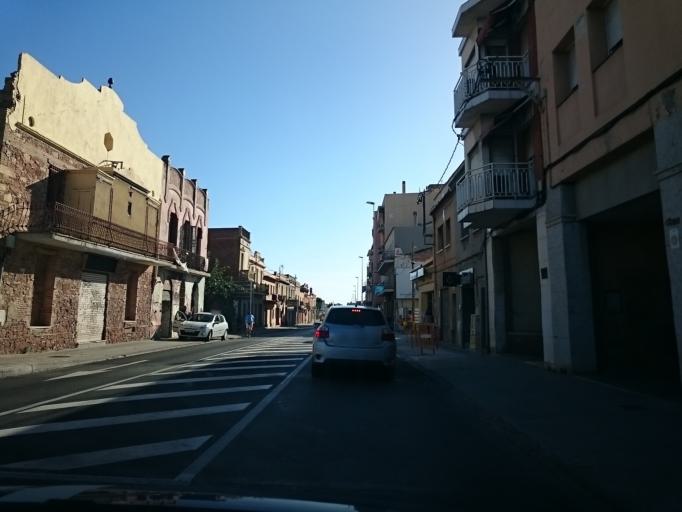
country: ES
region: Catalonia
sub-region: Provincia de Barcelona
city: Viladecans
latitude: 41.3154
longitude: 2.0204
